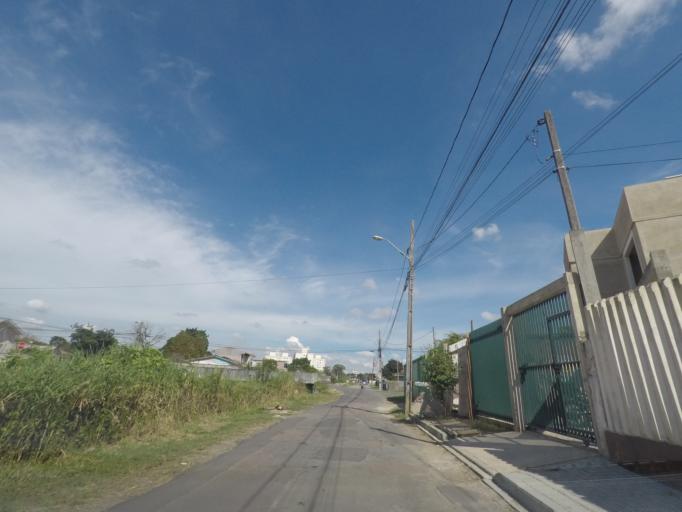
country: BR
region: Parana
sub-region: Curitiba
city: Curitiba
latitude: -25.4772
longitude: -49.2693
